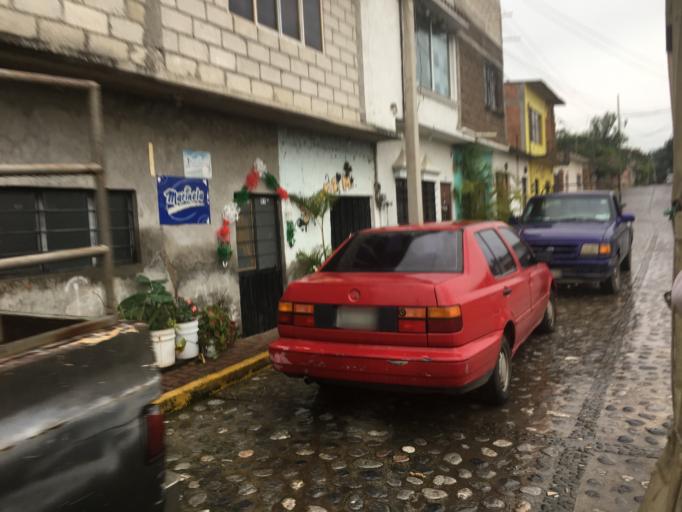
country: MX
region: Morelos
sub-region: Tlayacapan
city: Tlayacapan
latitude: 18.9598
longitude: -98.9798
